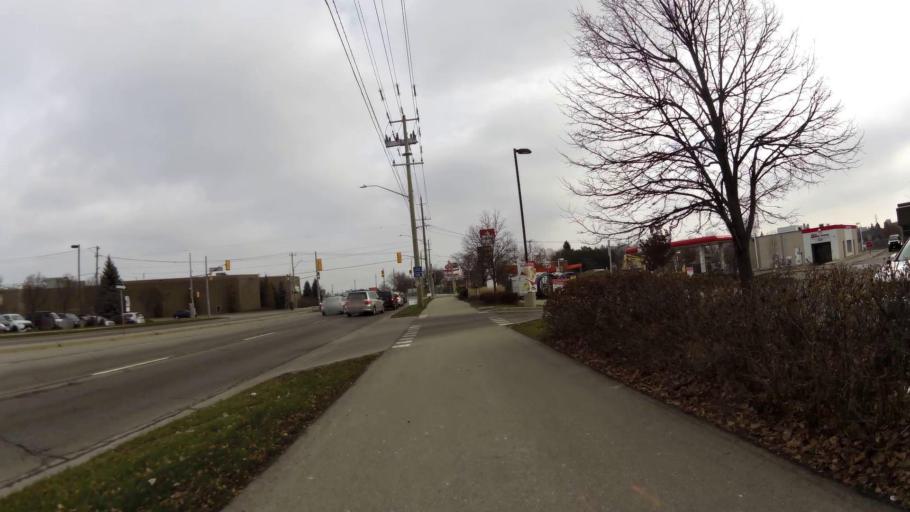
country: CA
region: Ontario
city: Kitchener
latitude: 43.4225
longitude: -80.4885
